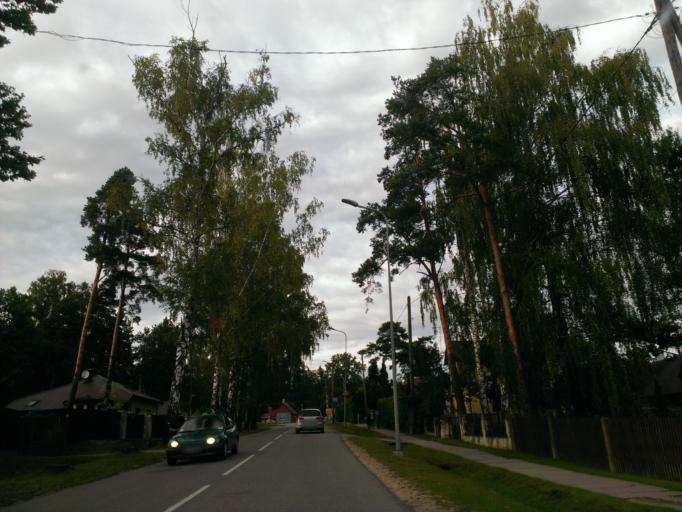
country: LV
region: Ogre
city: Ogre
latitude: 56.8205
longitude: 24.5813
